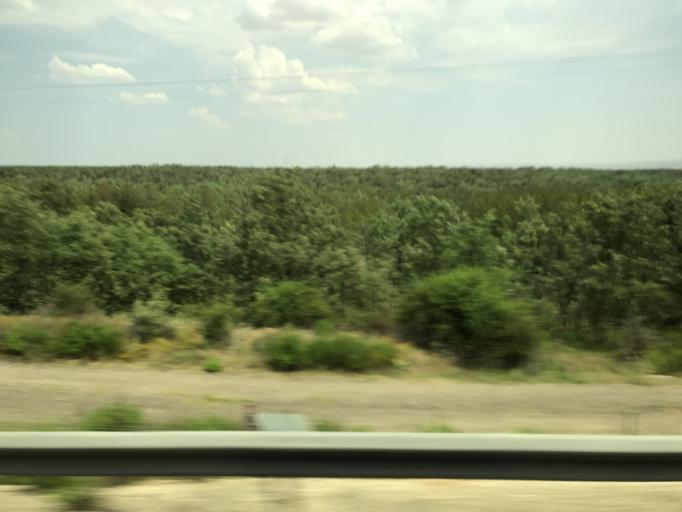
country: ES
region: Castille and Leon
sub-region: Provincia de Segovia
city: Fresno de la Fuente
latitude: 41.4118
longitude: -3.6567
